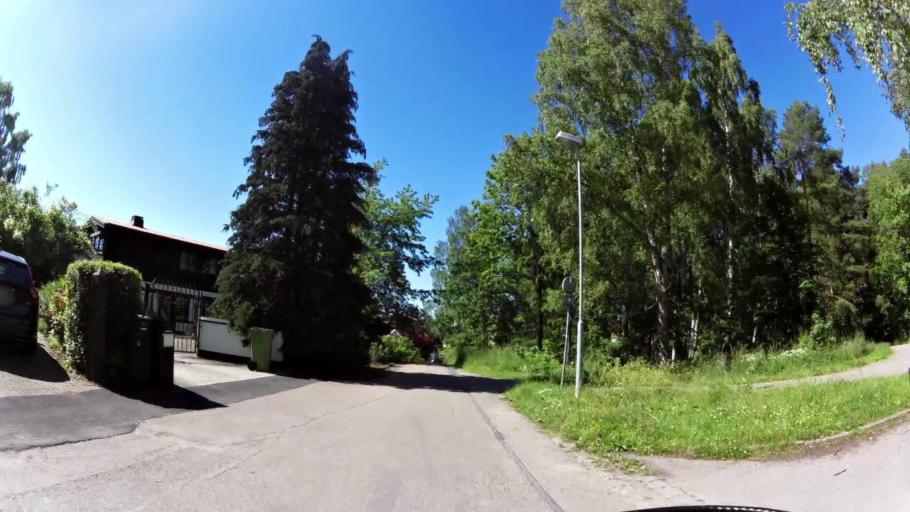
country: SE
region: OEstergoetland
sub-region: Linkopings Kommun
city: Linkoping
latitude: 58.4013
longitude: 15.6291
